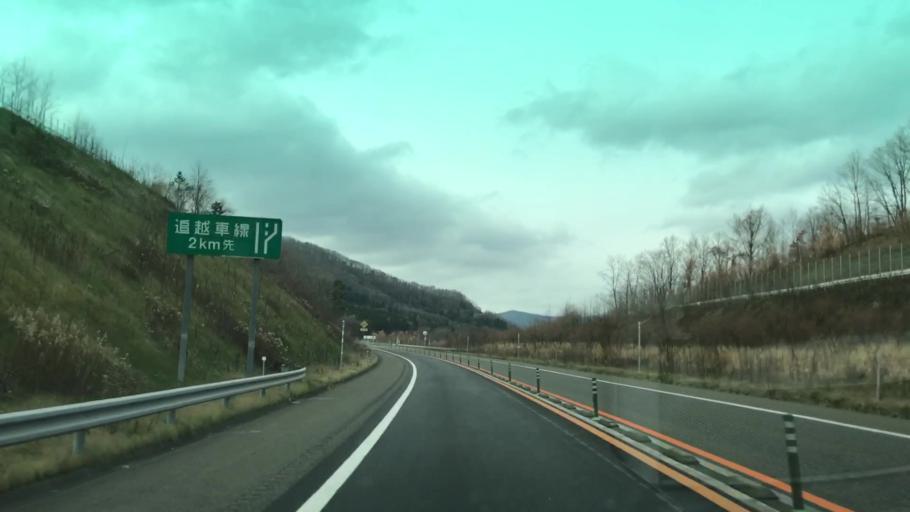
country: JP
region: Hokkaido
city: Otofuke
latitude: 43.0064
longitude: 142.8425
